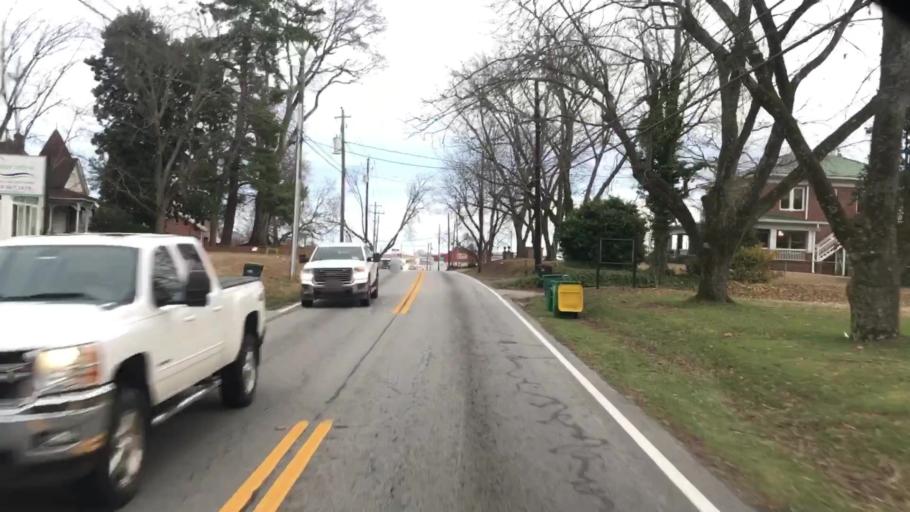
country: US
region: Georgia
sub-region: Barrow County
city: Winder
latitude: 33.9967
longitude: -83.7394
